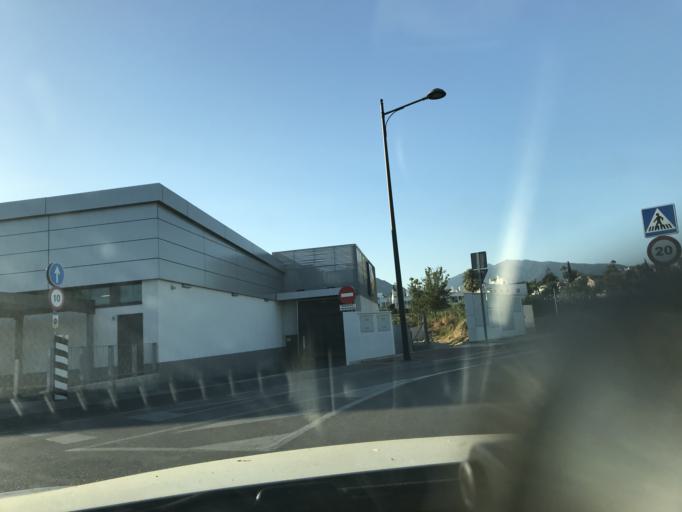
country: ES
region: Andalusia
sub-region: Provincia de Malaga
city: Benahavis
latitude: 36.4632
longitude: -5.0427
